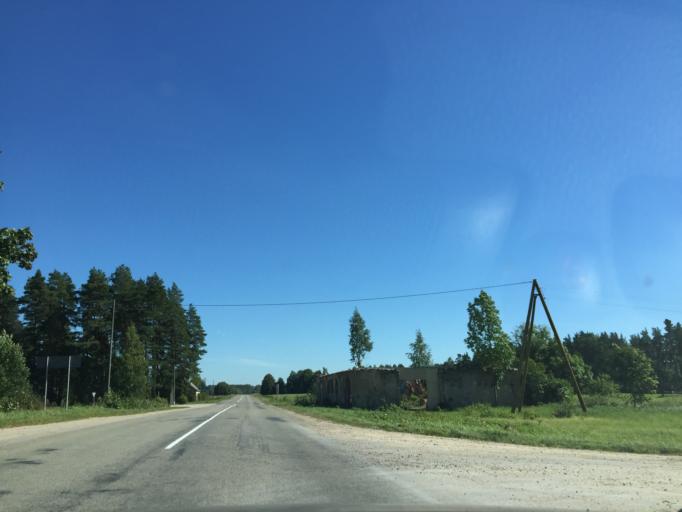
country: LV
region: Akniste
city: Akniste
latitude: 56.1466
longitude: 25.7920
